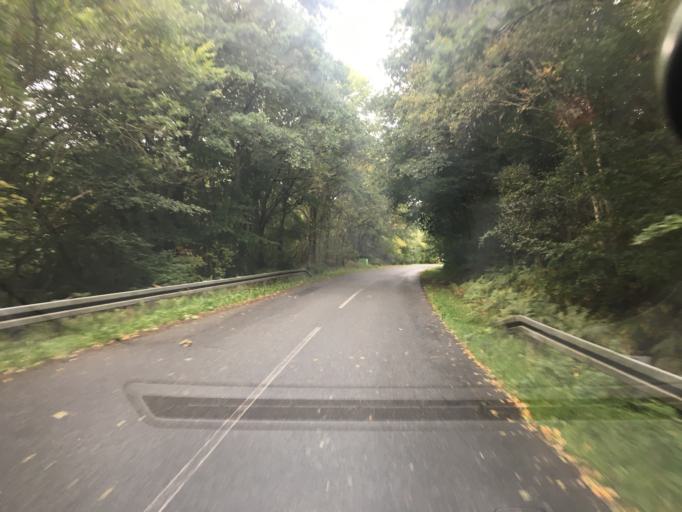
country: DK
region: South Denmark
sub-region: Tonder Kommune
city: Logumkloster
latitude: 55.0941
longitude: 8.9306
